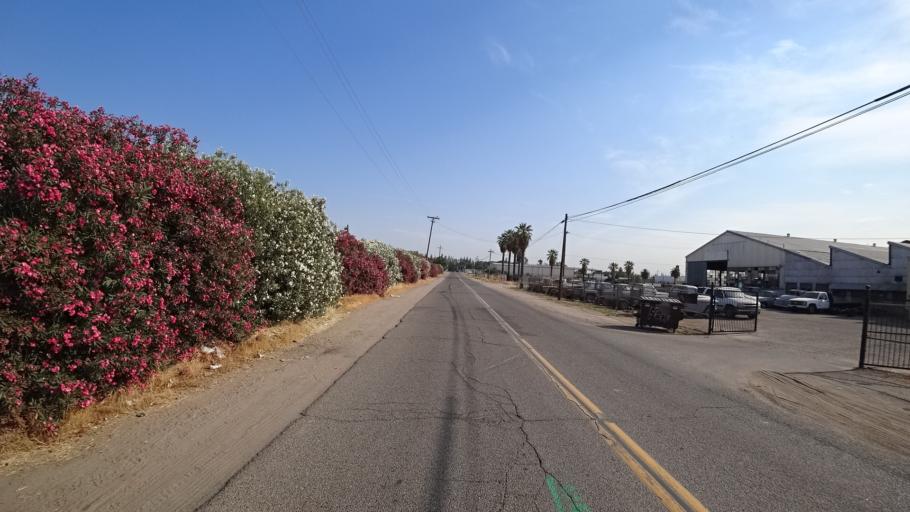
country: US
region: California
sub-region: Fresno County
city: Fresno
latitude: 36.7444
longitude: -119.8176
